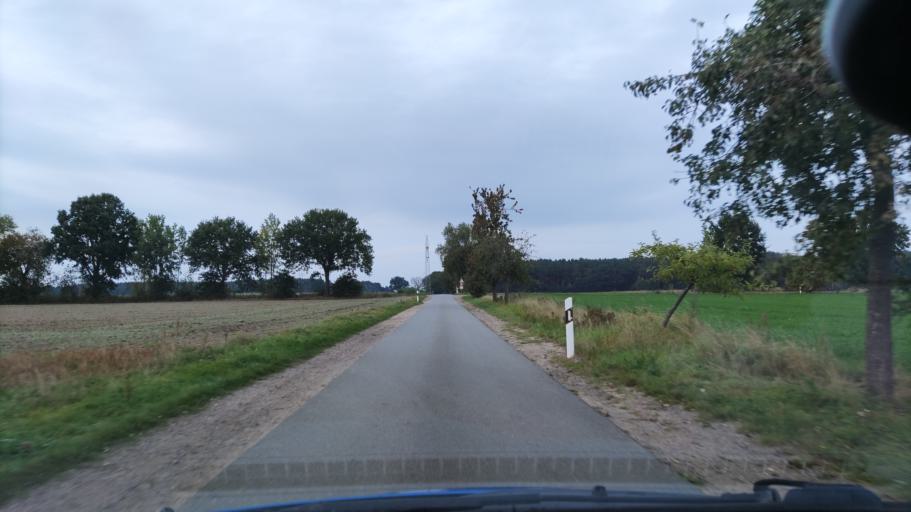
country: DE
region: Lower Saxony
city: Karwitz
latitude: 53.0944
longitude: 11.0145
